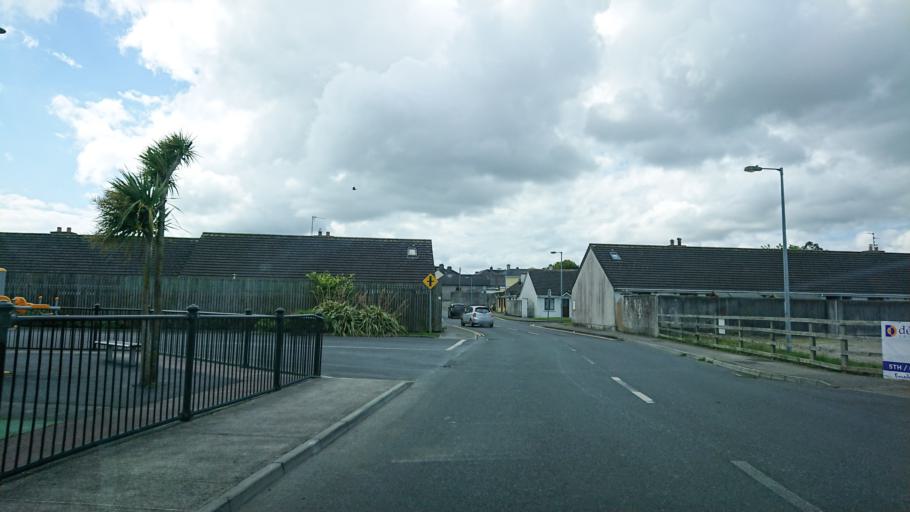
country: IE
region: Munster
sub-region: Waterford
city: Dungarvan
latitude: 52.0921
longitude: -7.6293
